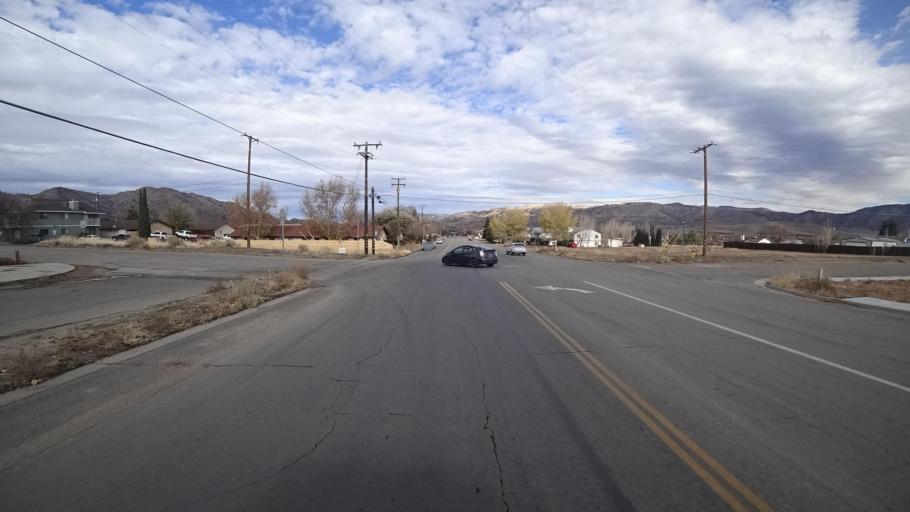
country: US
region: California
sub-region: Kern County
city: Golden Hills
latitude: 35.1253
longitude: -118.4860
